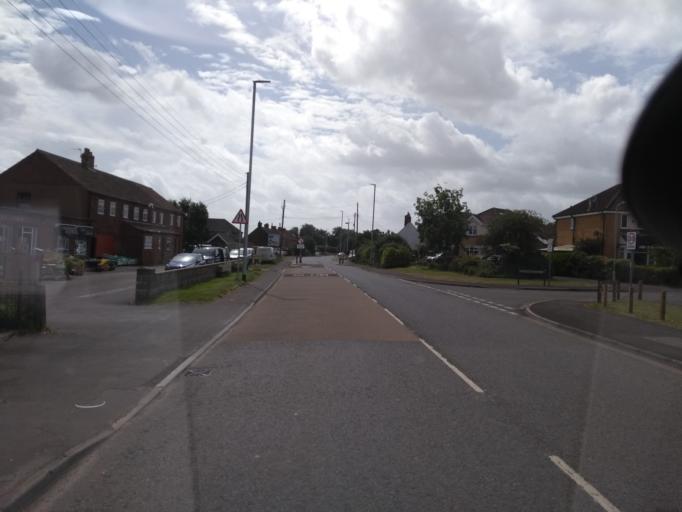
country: GB
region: England
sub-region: Somerset
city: Bridgwater
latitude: 51.1469
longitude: -3.0599
